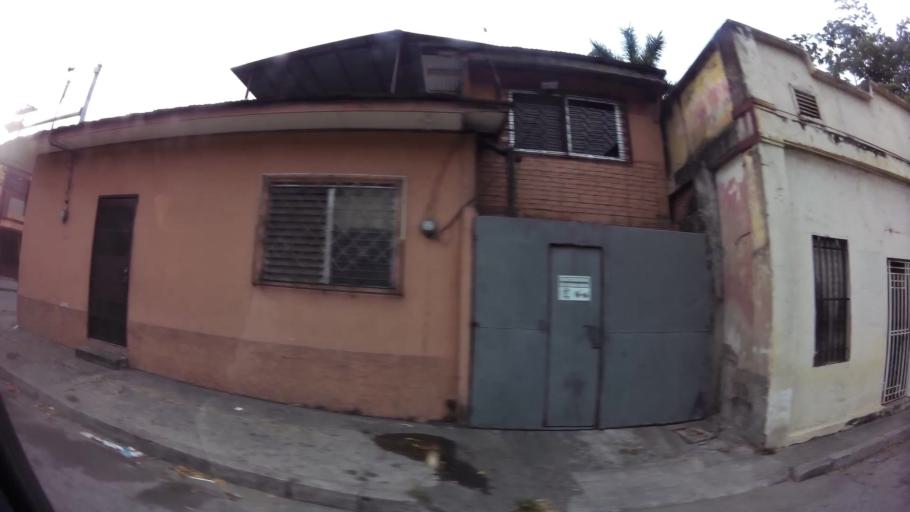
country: HN
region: Cortes
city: San Pedro Sula
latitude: 15.5111
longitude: -88.0247
